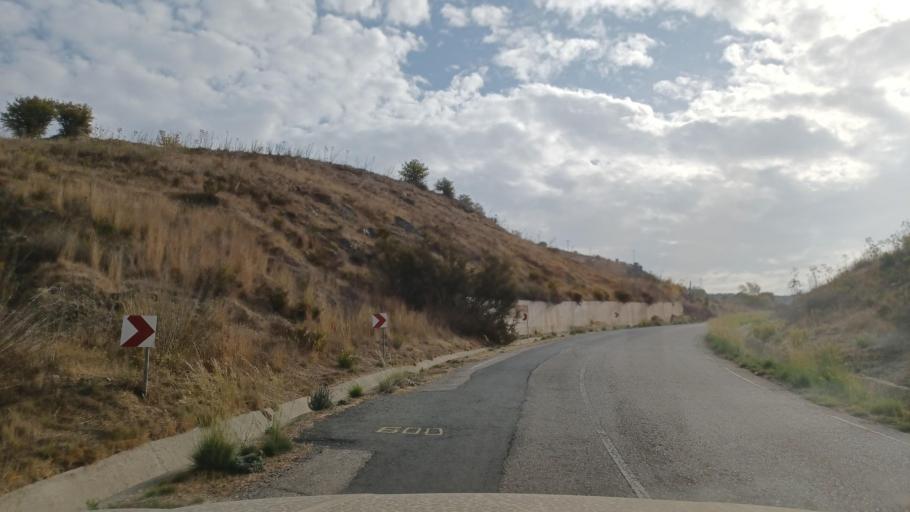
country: CY
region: Pafos
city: Mesogi
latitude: 34.8013
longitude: 32.4991
